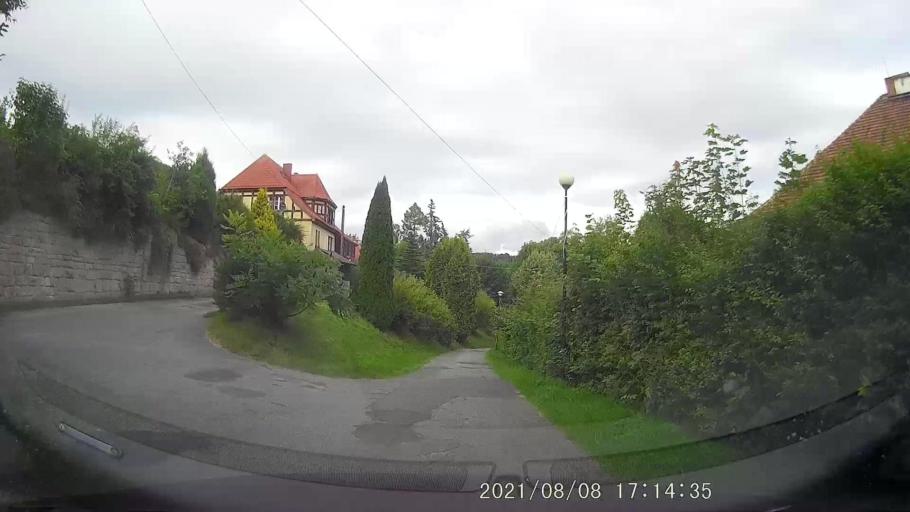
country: PL
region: Lower Silesian Voivodeship
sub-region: Powiat klodzki
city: Duszniki-Zdroj
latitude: 50.4014
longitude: 16.3872
